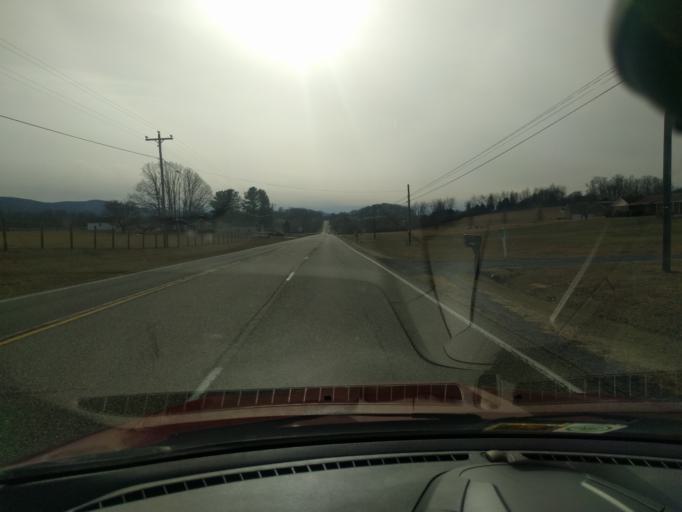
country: US
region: Virginia
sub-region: Augusta County
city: Stuarts Draft
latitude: 37.9671
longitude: -79.1775
